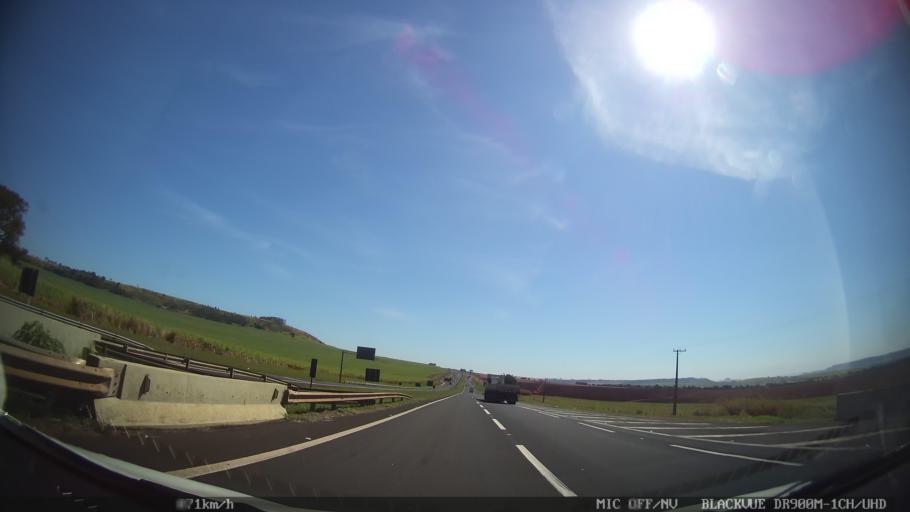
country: BR
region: Sao Paulo
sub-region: Cravinhos
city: Cravinhos
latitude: -21.4116
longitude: -47.6663
